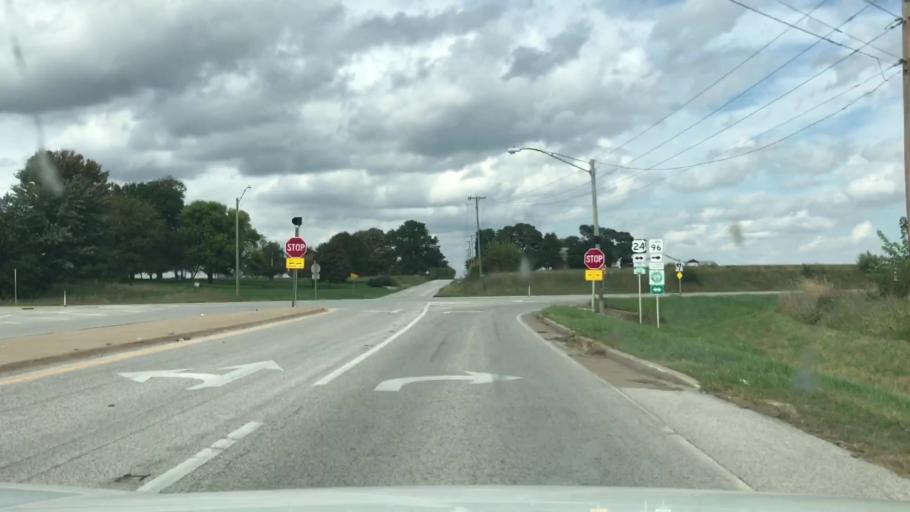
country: US
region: Illinois
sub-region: Adams County
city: Quincy
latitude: 40.0018
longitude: -91.3769
